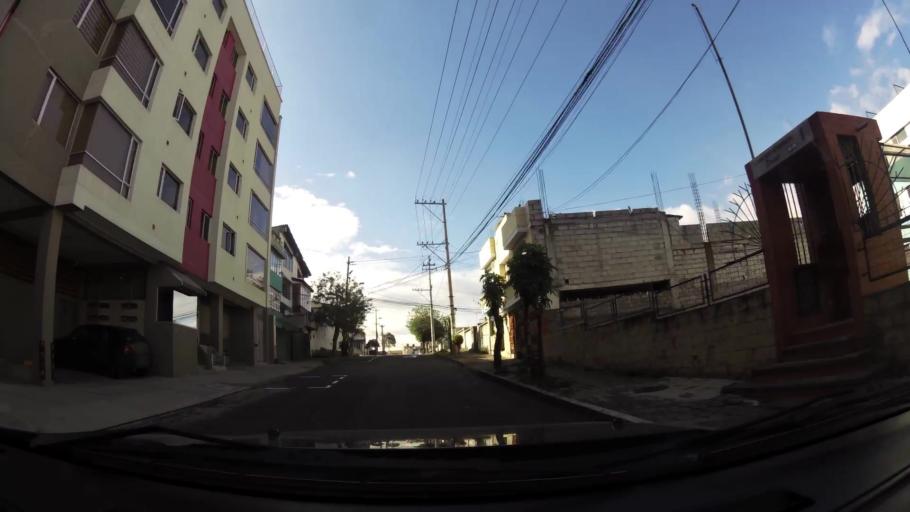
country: EC
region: Pichincha
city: Quito
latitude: -0.2168
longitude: -78.4924
